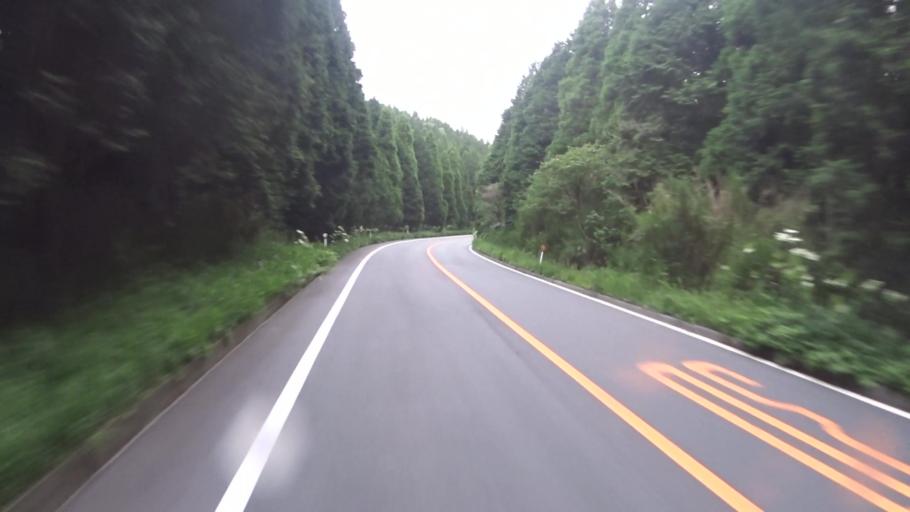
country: JP
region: Kumamoto
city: Ozu
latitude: 32.9186
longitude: 130.9675
